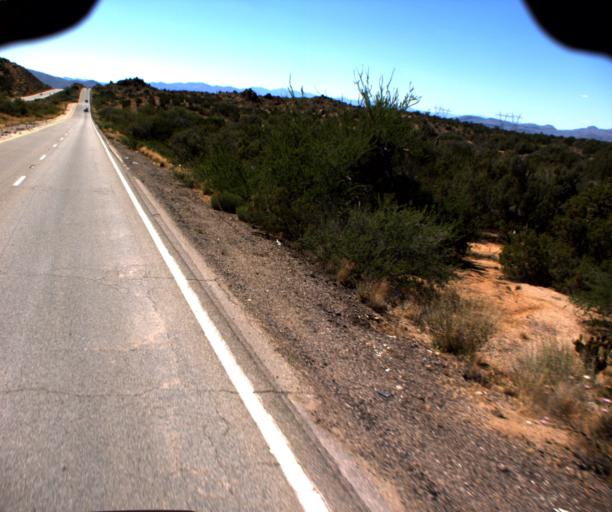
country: US
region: Arizona
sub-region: Yavapai County
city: Bagdad
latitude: 34.4796
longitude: -113.3371
